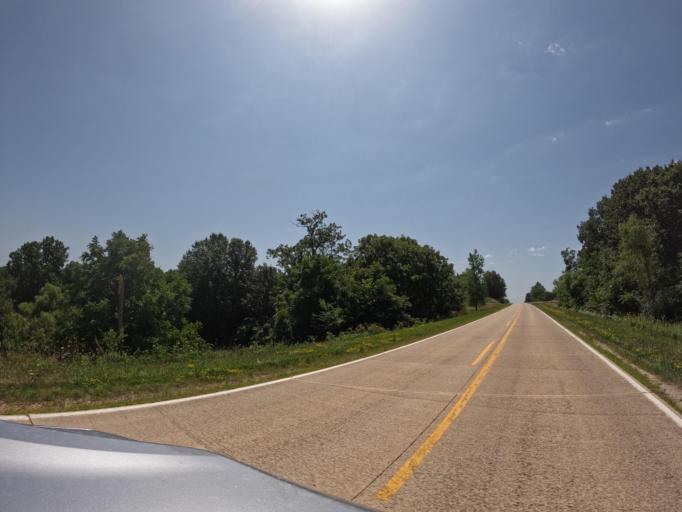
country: US
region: Iowa
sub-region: Henry County
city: Mount Pleasant
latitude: 40.9489
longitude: -91.5546
